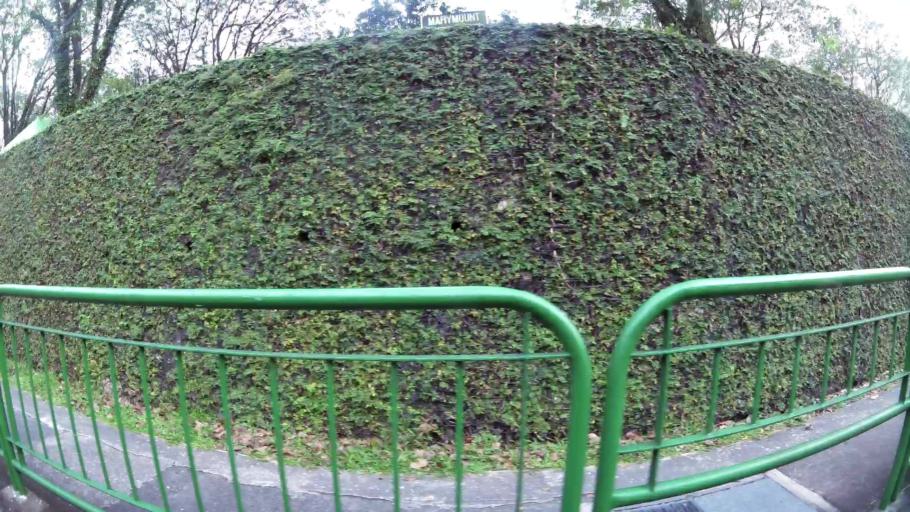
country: SG
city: Singapore
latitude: 1.3392
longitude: 103.8377
